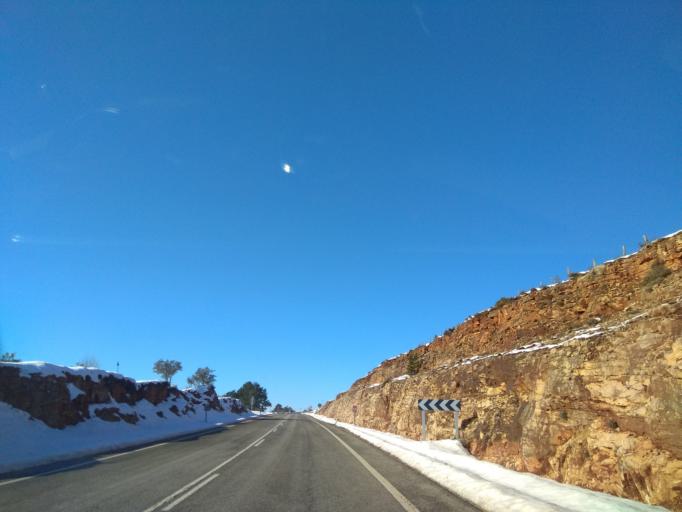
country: ES
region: Castille and Leon
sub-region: Provincia de Burgos
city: Medina de Pomar
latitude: 42.9376
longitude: -3.6642
